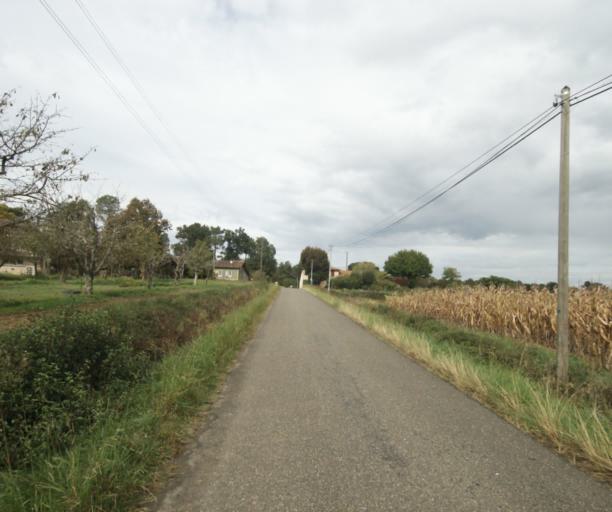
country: FR
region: Midi-Pyrenees
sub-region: Departement du Gers
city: Cazaubon
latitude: 43.8802
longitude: -0.1005
